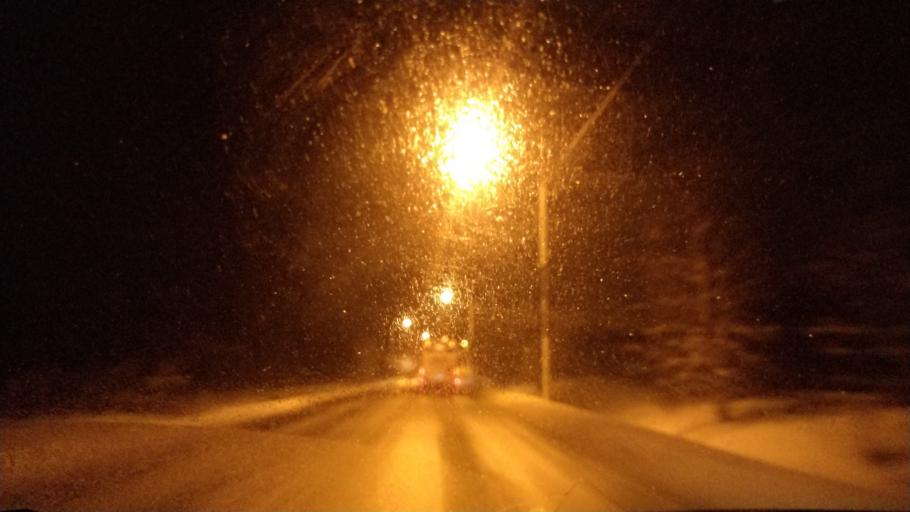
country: FI
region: Lapland
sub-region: Rovaniemi
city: Rovaniemi
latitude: 66.2929
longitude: 25.3505
